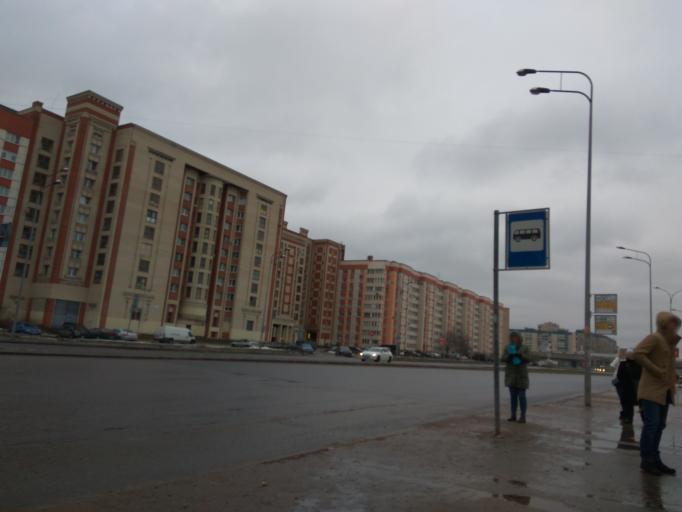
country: RU
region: Leningrad
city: Untolovo
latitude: 60.0049
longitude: 30.2250
